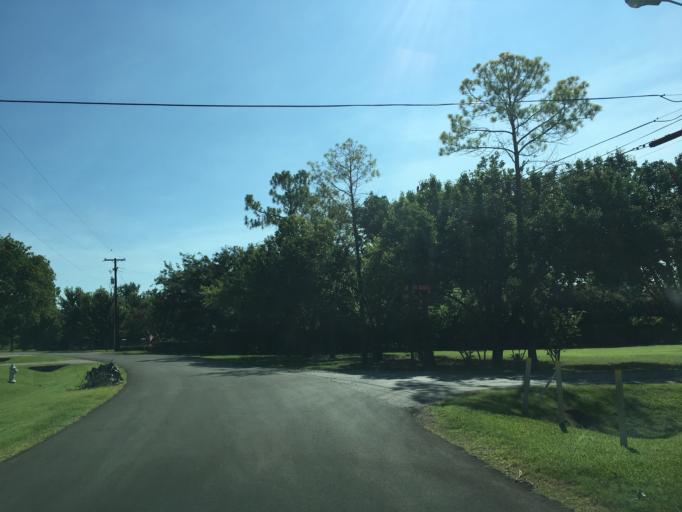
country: US
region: Texas
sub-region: Dallas County
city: Farmers Branch
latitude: 32.9216
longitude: -96.8699
